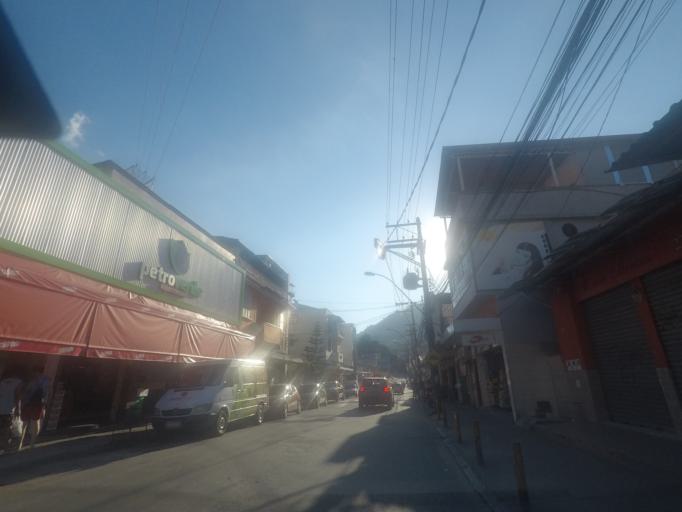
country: BR
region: Rio de Janeiro
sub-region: Petropolis
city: Petropolis
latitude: -22.4890
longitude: -43.1529
